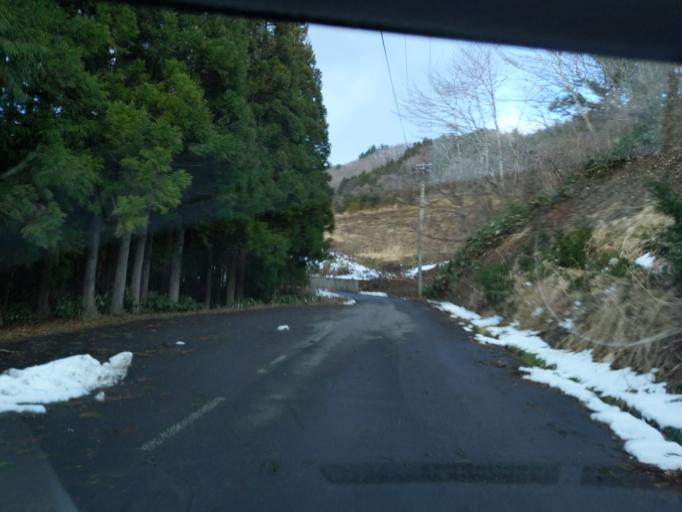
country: JP
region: Iwate
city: Ichinoseki
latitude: 39.0102
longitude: 140.9795
